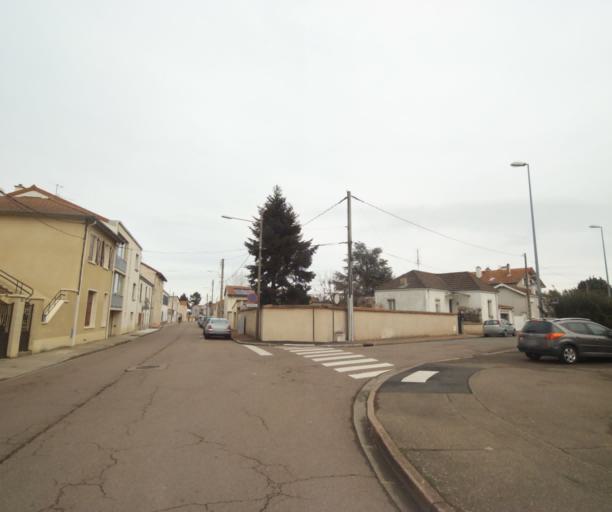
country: FR
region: Rhone-Alpes
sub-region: Departement de la Loire
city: Riorges
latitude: 46.0293
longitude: 4.0533
